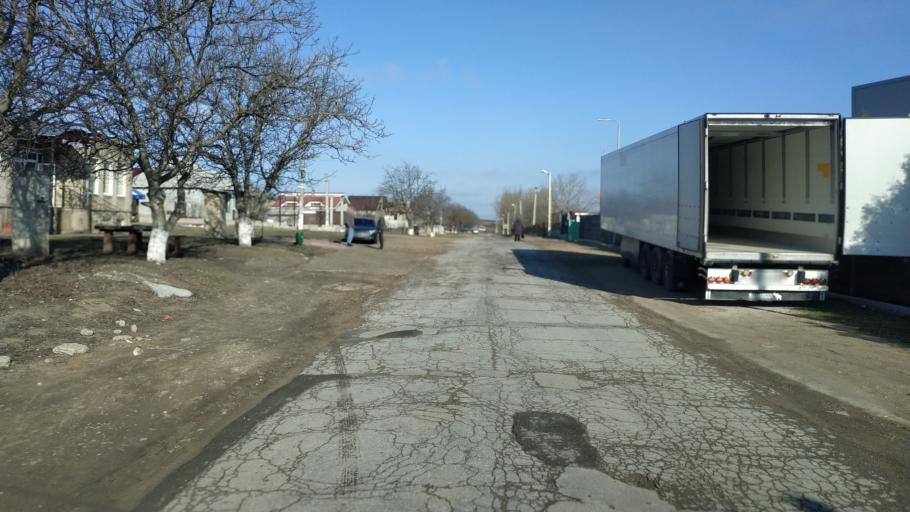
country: MD
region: Laloveni
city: Ialoveni
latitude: 46.9452
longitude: 28.7223
